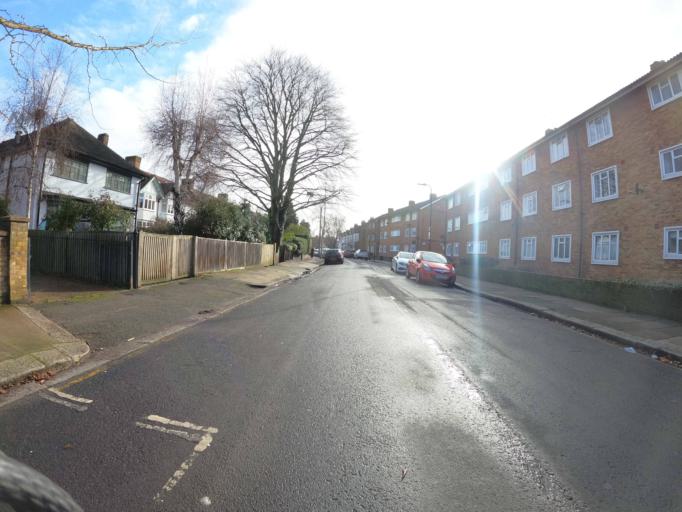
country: GB
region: England
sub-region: Greater London
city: Acton
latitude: 51.5023
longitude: -0.2618
